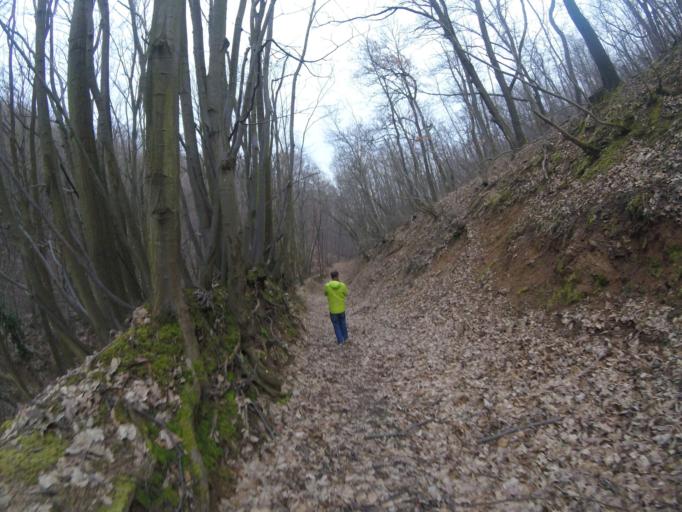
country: HU
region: Baranya
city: Mecseknadasd
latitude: 46.1418
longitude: 18.5175
